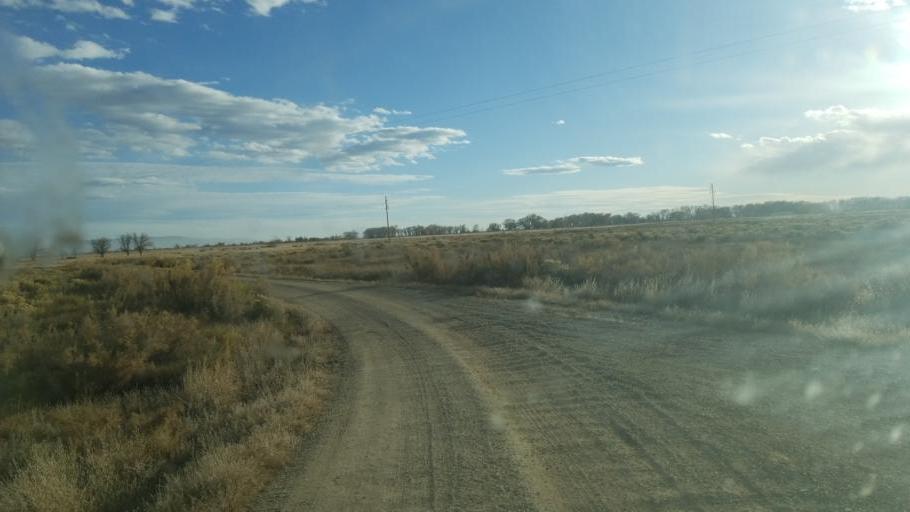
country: US
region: Colorado
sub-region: Alamosa County
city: Alamosa East
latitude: 37.4608
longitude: -105.8344
